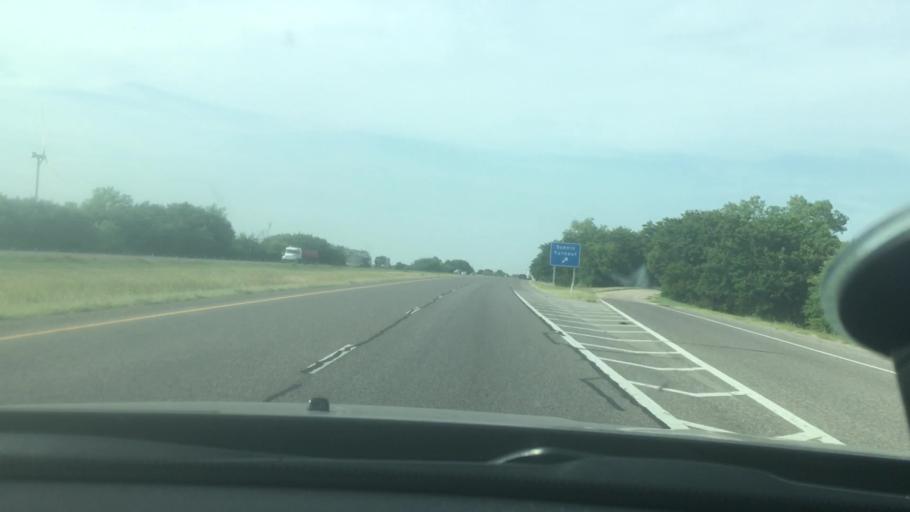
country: US
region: Oklahoma
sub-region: Murray County
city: Davis
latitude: 34.3850
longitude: -97.1423
